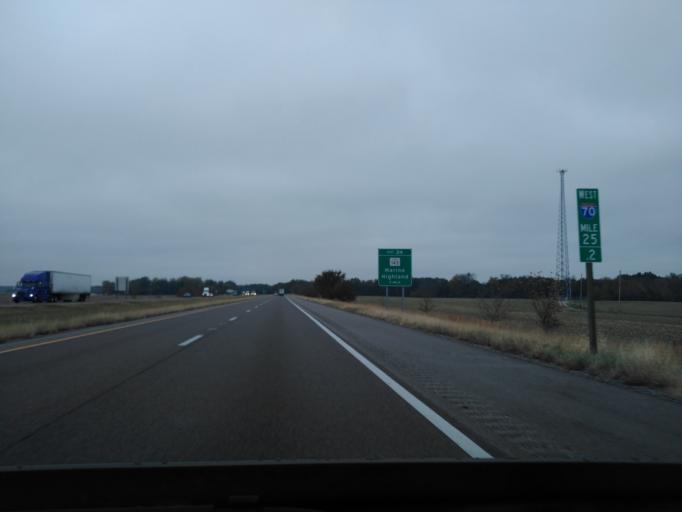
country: US
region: Illinois
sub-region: Madison County
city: Highland
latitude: 38.7850
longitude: -89.7231
